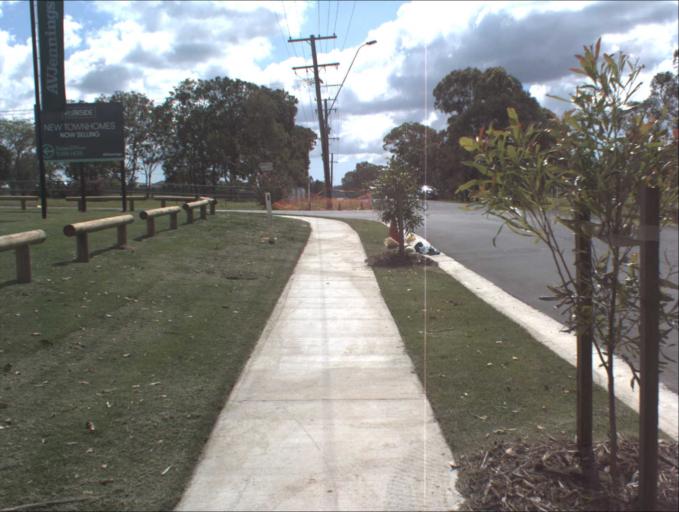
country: AU
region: Queensland
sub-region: Logan
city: Waterford West
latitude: -27.6840
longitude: 153.1581
